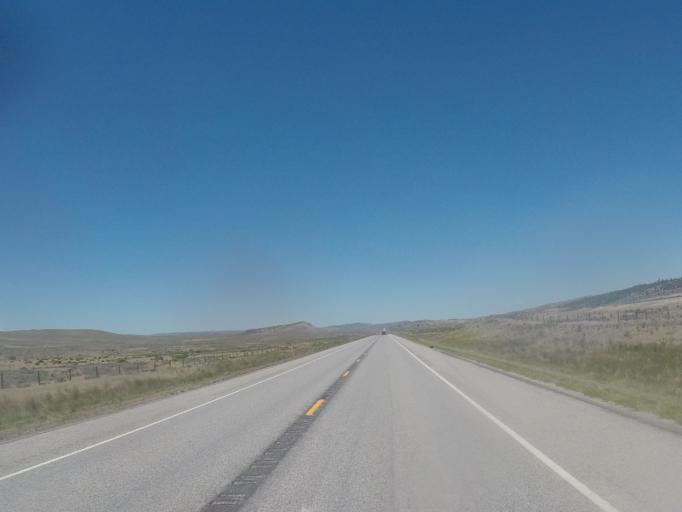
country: US
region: Montana
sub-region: Carbon County
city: Red Lodge
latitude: 45.1784
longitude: -108.8427
